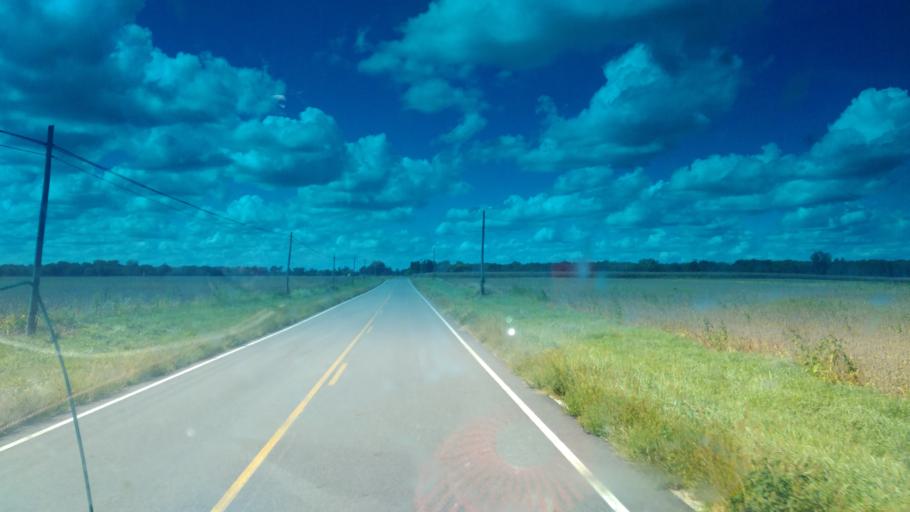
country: US
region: Ohio
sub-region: Union County
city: Marysville
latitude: 40.1853
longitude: -83.4551
